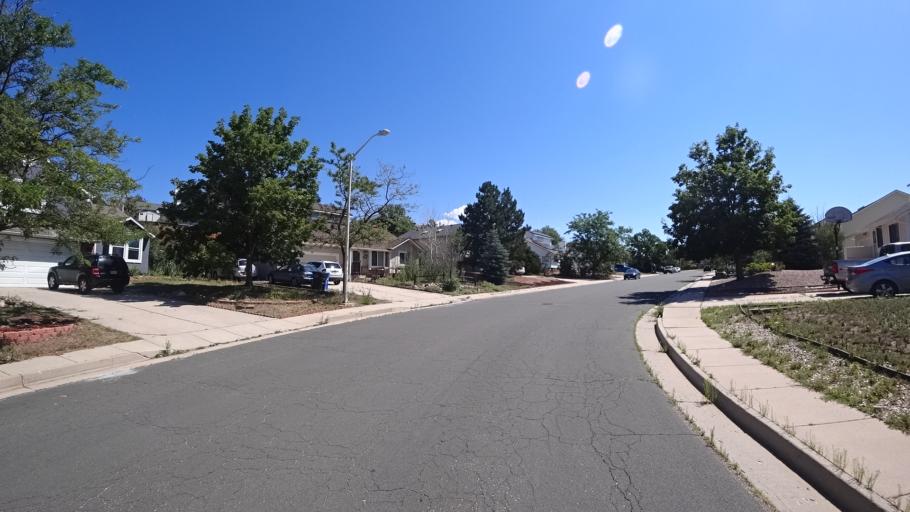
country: US
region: Colorado
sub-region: El Paso County
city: Black Forest
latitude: 38.9384
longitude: -104.7653
